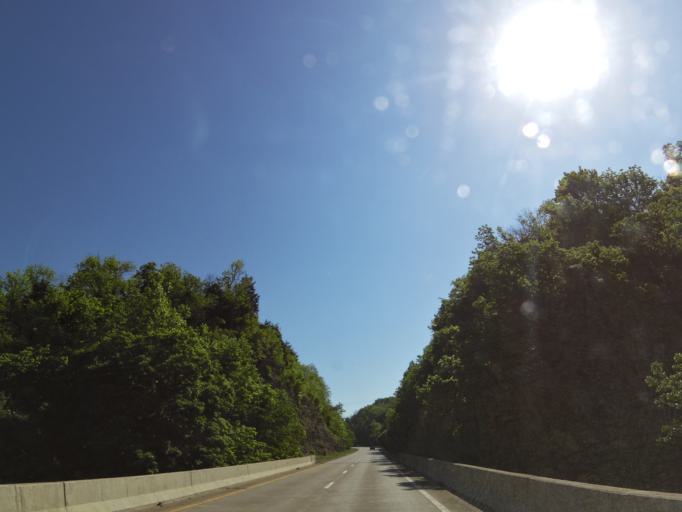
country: US
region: Kentucky
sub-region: Franklin County
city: Frankfort
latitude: 38.1611
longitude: -84.8512
